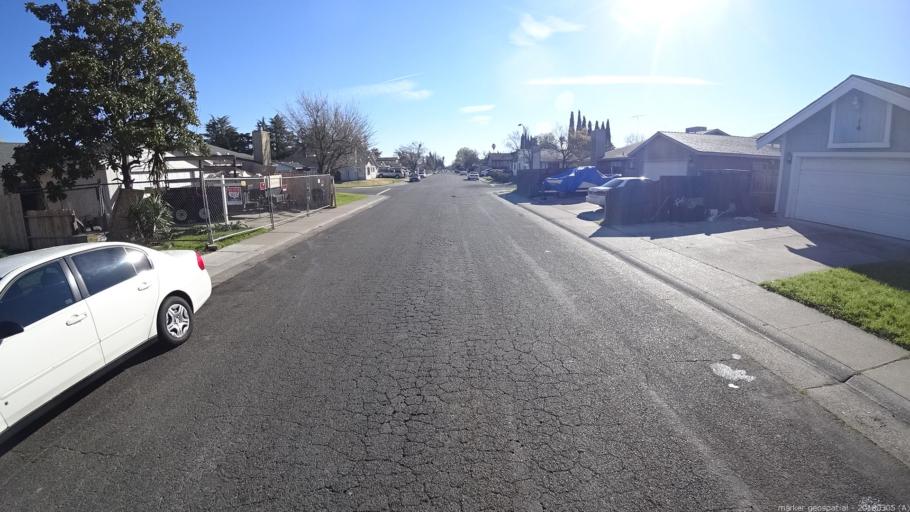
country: US
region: California
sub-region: Sacramento County
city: Florin
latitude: 38.4865
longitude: -121.4167
